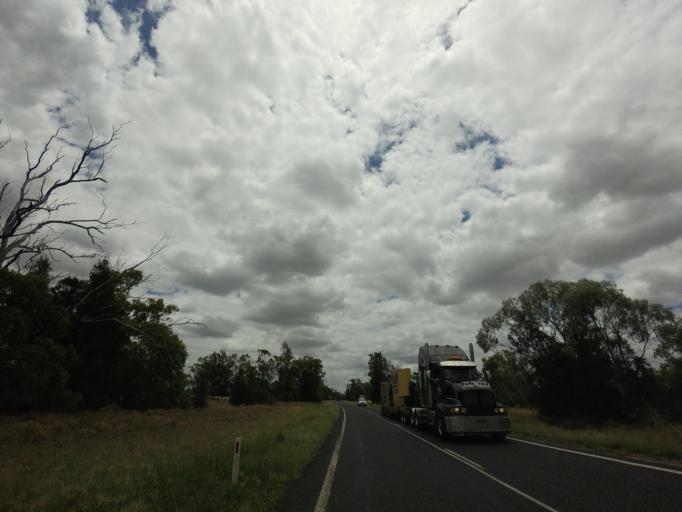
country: AU
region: Queensland
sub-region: Goondiwindi
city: Goondiwindi
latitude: -28.4968
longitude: 150.2922
